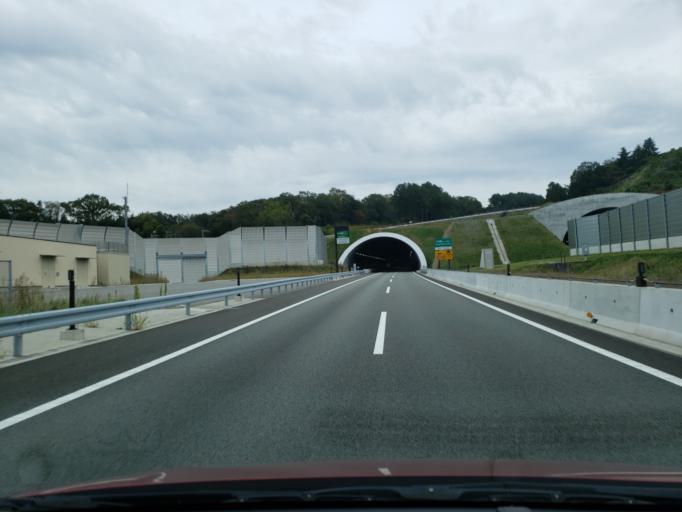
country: JP
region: Osaka
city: Ikeda
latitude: 34.8816
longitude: 135.4083
